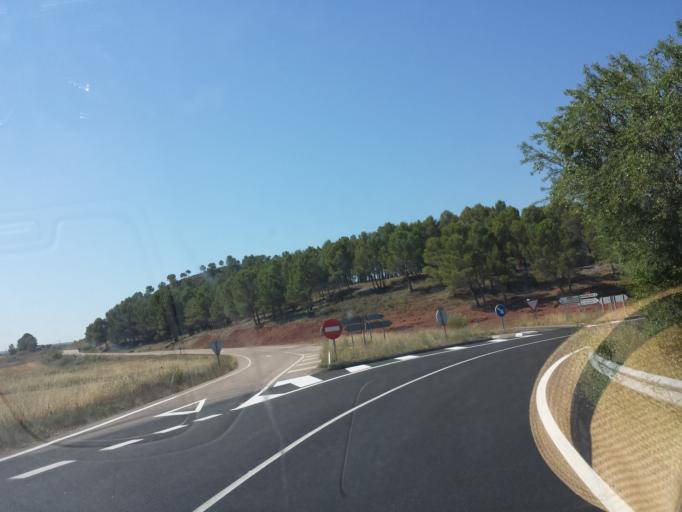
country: ES
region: Aragon
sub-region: Provincia de Zaragoza
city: Nuevalos
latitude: 41.2116
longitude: -1.7753
